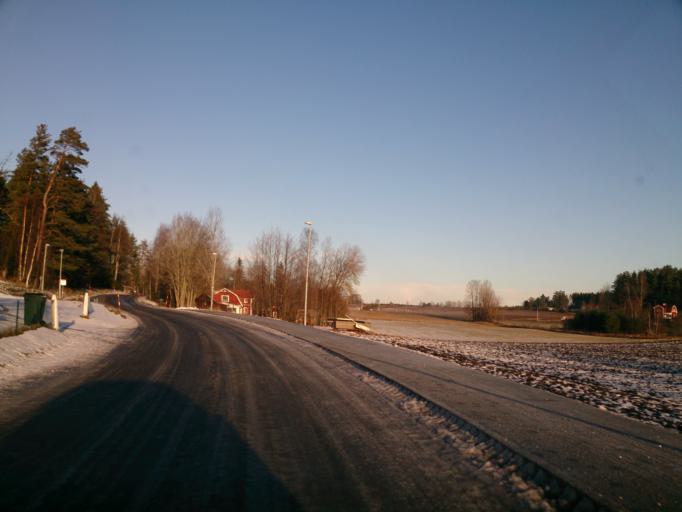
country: SE
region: OEstergoetland
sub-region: Linkopings Kommun
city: Sturefors
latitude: 58.3101
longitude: 15.8731
